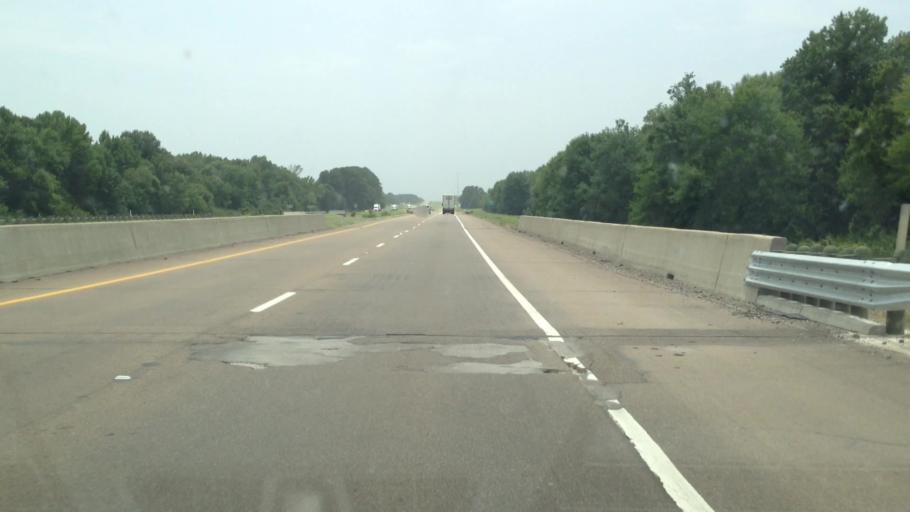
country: US
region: Texas
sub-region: Bowie County
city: De Kalb
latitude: 33.4269
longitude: -94.5429
